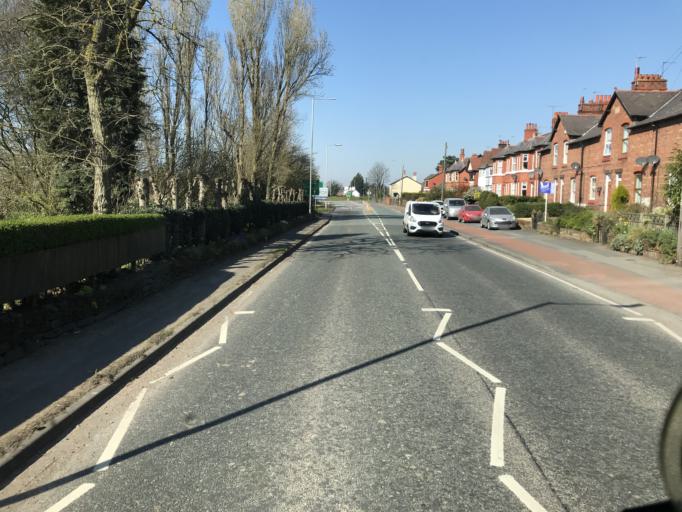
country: GB
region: England
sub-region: Cheshire West and Chester
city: Guilden Sutton
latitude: 53.1867
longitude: -2.8501
